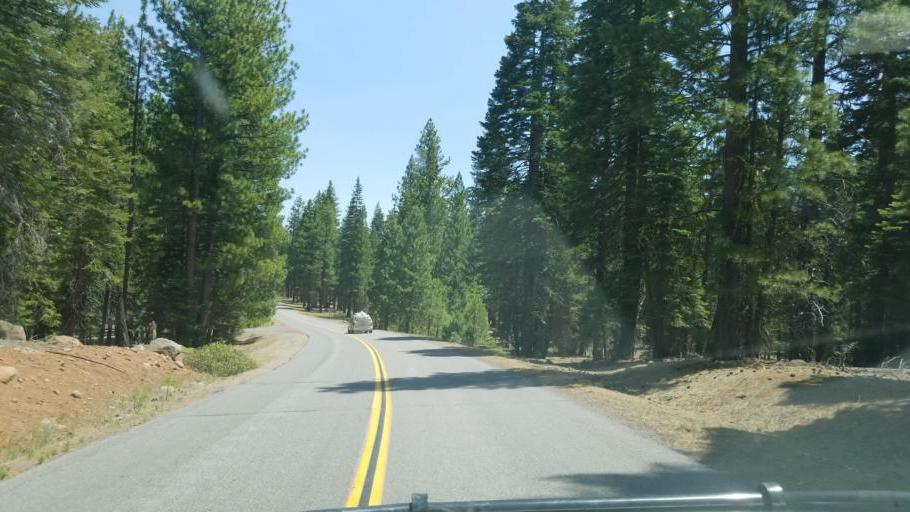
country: US
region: California
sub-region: Lassen County
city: Susanville
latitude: 40.5495
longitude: -120.8158
